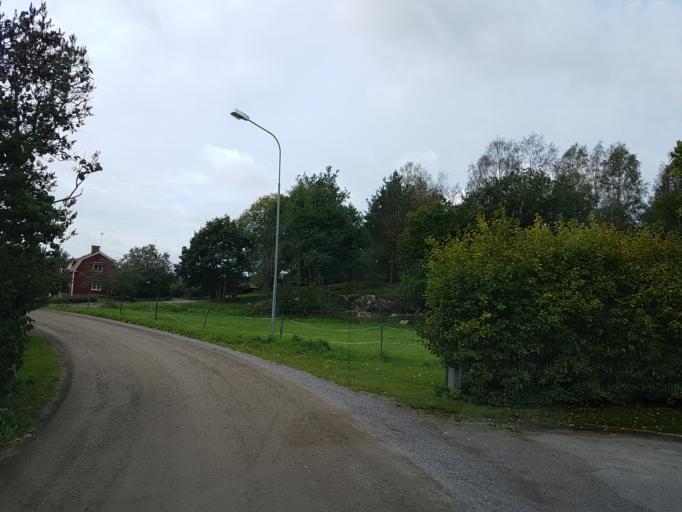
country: SE
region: OEstergoetland
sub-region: Atvidabergs Kommun
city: Atvidaberg
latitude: 58.2154
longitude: 16.0253
